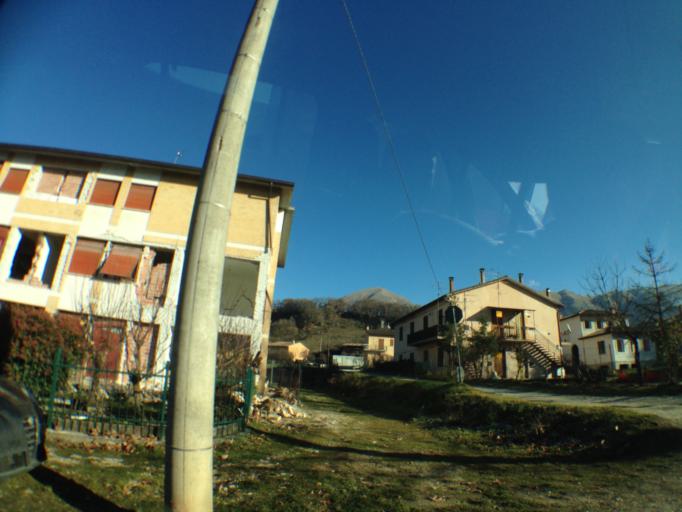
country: IT
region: Umbria
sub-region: Provincia di Perugia
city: Norcia
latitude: 42.7978
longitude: 13.0961
